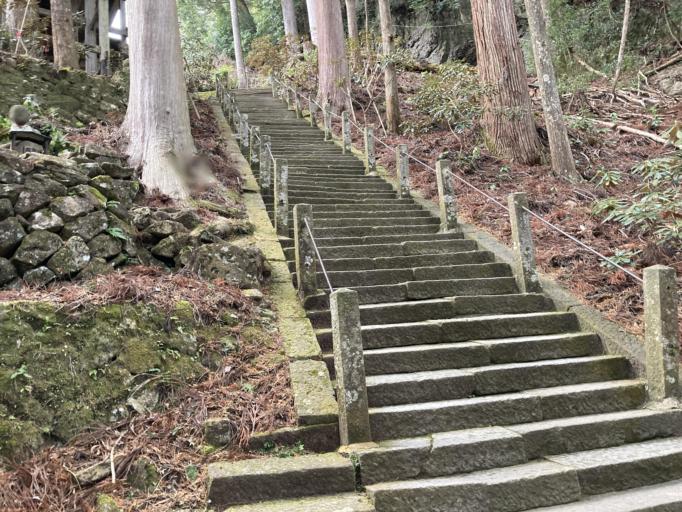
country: JP
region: Mie
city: Nabari
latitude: 34.5399
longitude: 136.0391
